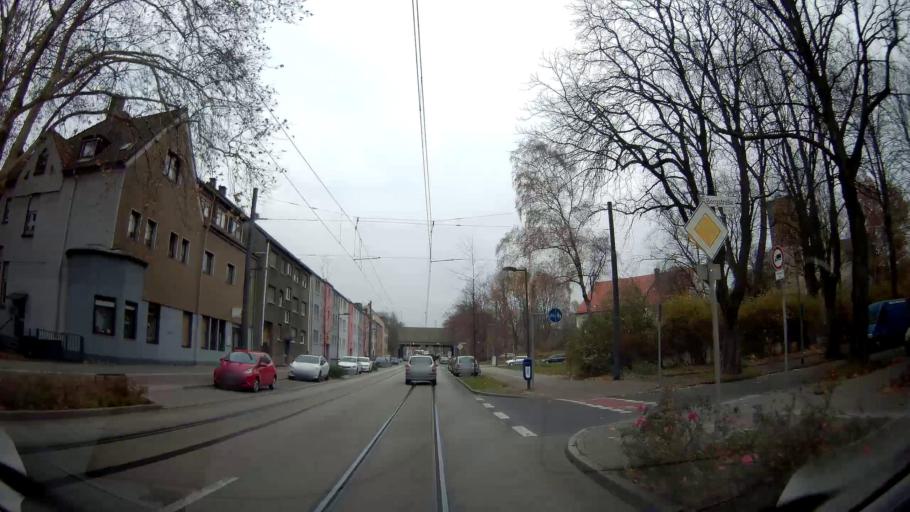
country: DE
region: North Rhine-Westphalia
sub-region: Regierungsbezirk Munster
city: Gladbeck
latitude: 51.5575
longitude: 7.0458
